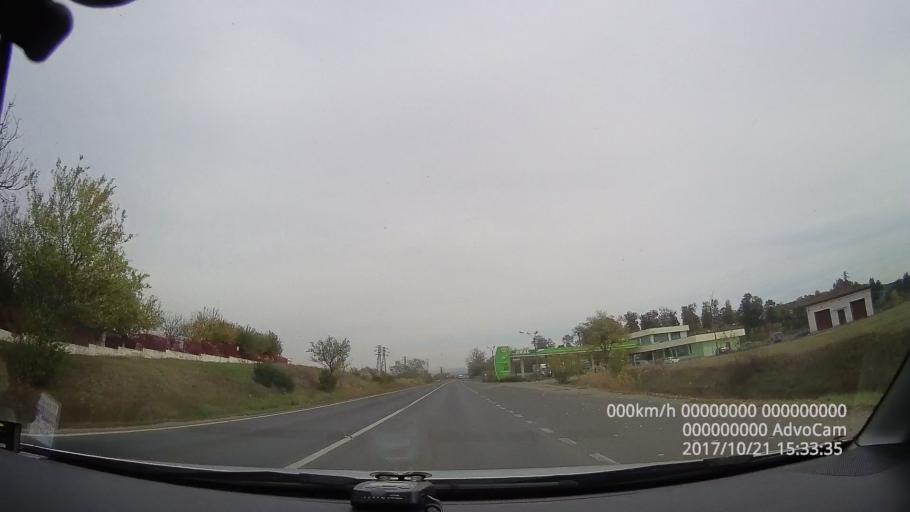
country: RO
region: Hunedoara
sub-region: Comuna Soimus
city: Soimus
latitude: 45.9063
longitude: 22.8768
